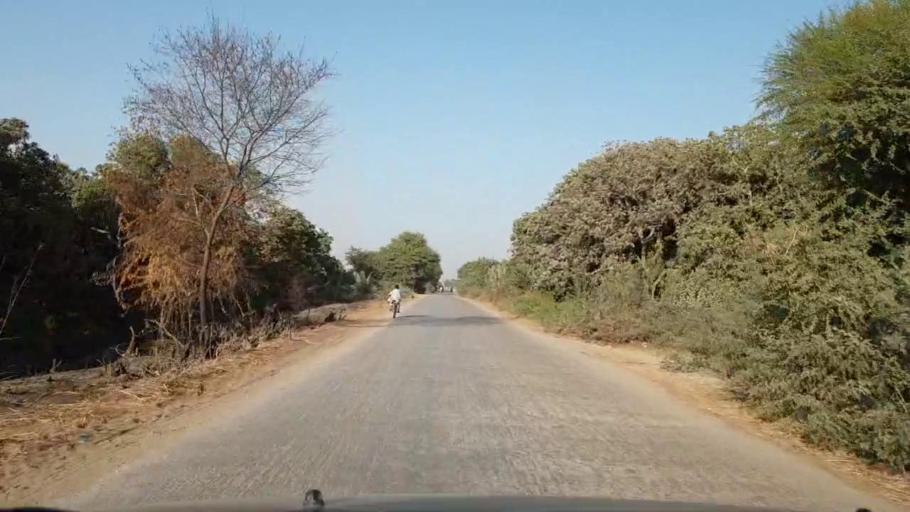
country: PK
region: Sindh
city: Chambar
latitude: 25.2196
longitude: 68.7806
